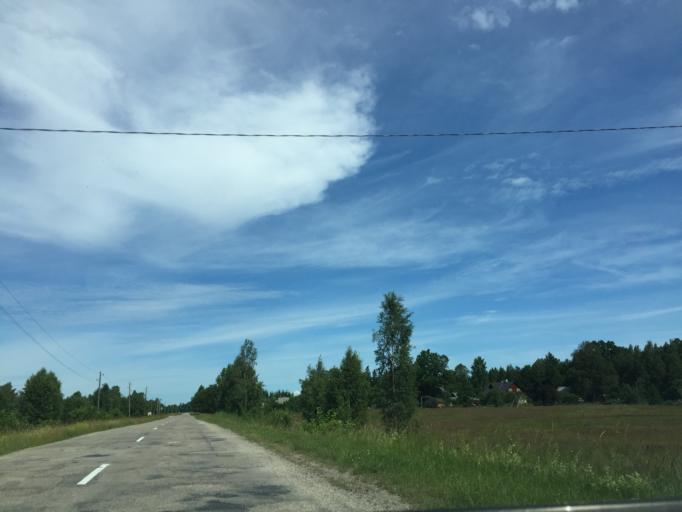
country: LV
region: Dundaga
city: Dundaga
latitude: 57.5235
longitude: 22.3320
